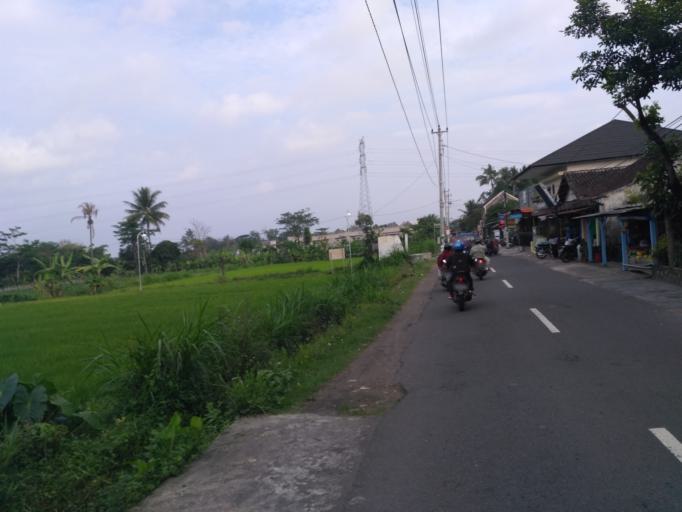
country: ID
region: Daerah Istimewa Yogyakarta
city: Melati
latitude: -7.7101
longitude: 110.3896
